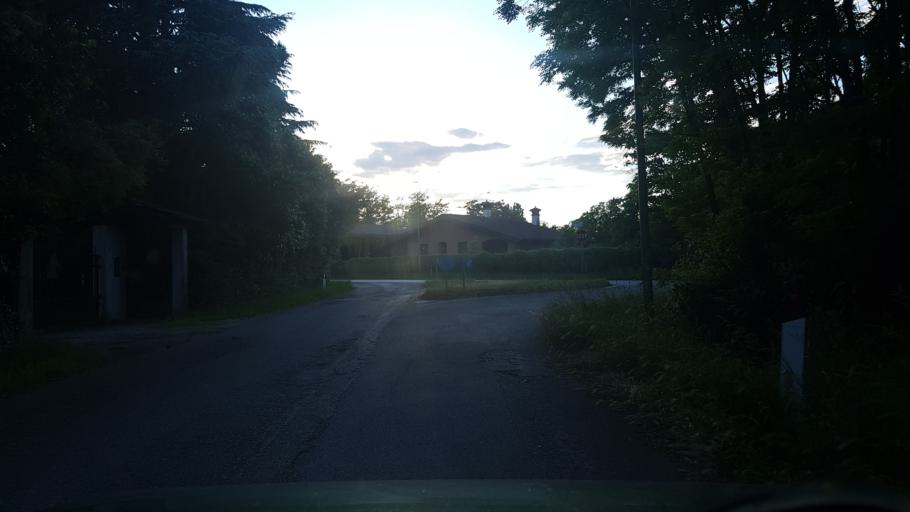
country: IT
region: Friuli Venezia Giulia
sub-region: Provincia di Udine
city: Palmanova
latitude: 45.9122
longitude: 13.3023
